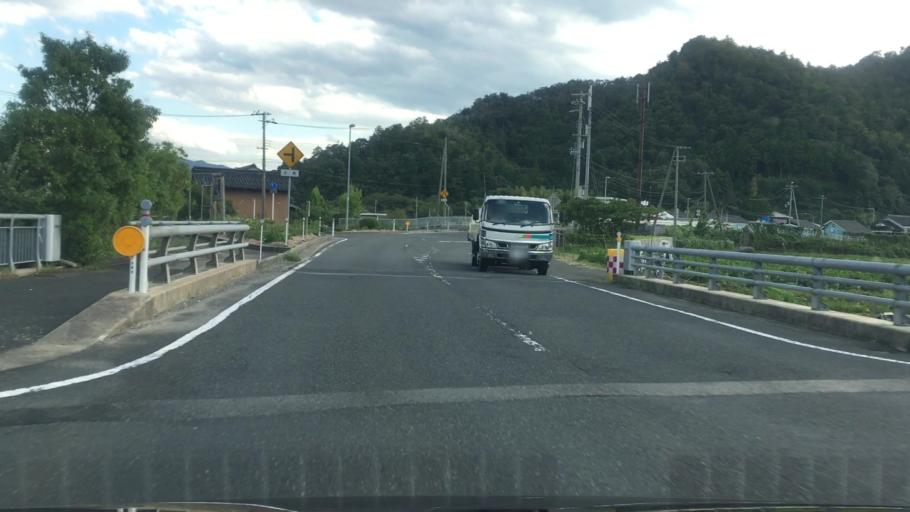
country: JP
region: Hyogo
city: Toyooka
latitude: 35.6103
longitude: 134.9194
